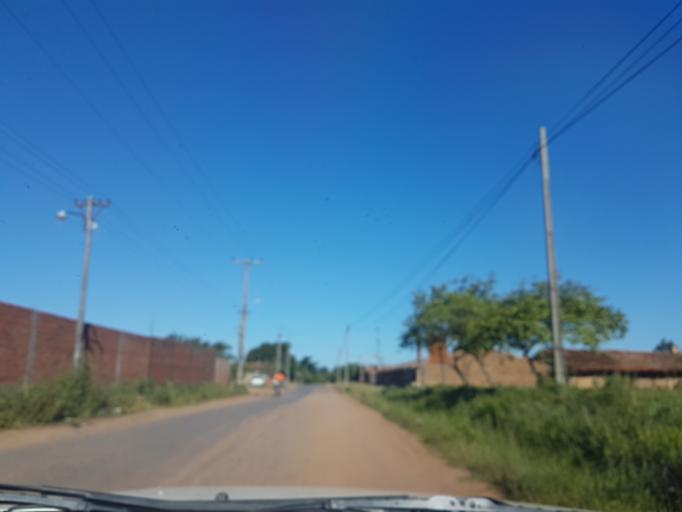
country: PY
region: Cordillera
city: Tobati
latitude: -25.2647
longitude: -57.0910
